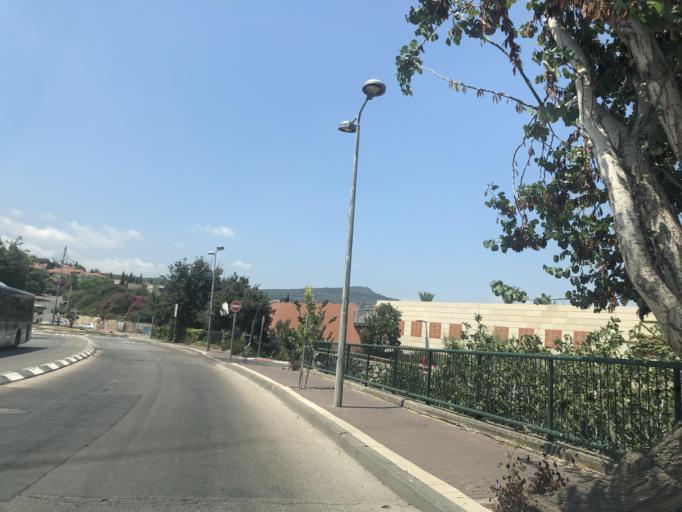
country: IL
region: Haifa
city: Daliyat el Karmil
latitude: 32.6421
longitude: 35.0919
